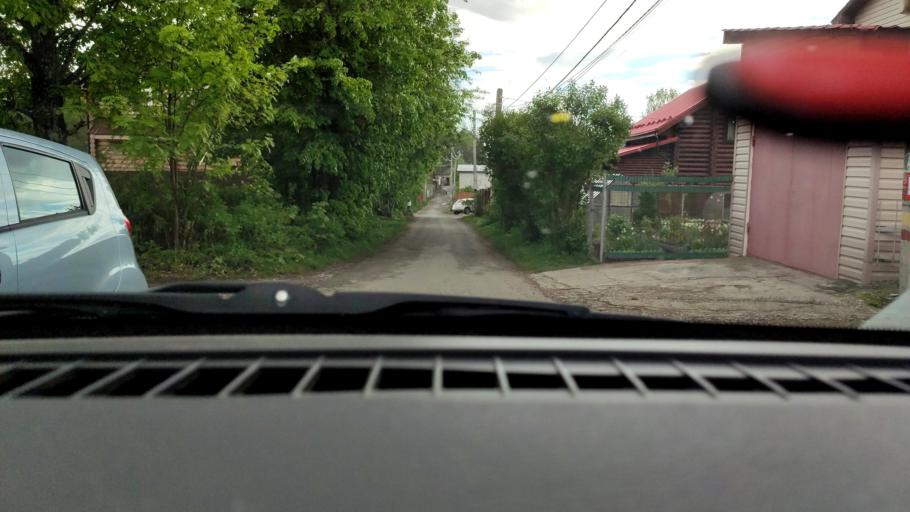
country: RU
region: Perm
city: Kondratovo
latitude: 58.0576
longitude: 56.1329
